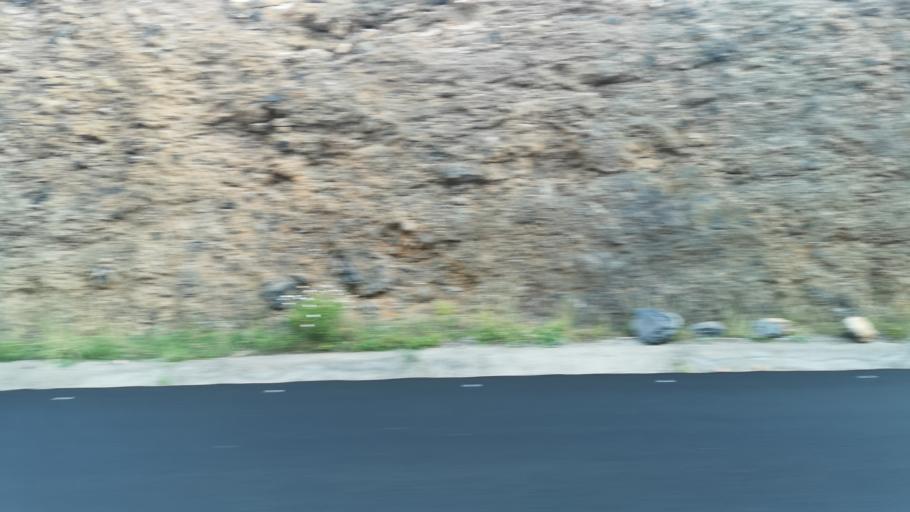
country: ES
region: Canary Islands
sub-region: Provincia de Santa Cruz de Tenerife
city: Alajero
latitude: 28.0525
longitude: -17.2005
